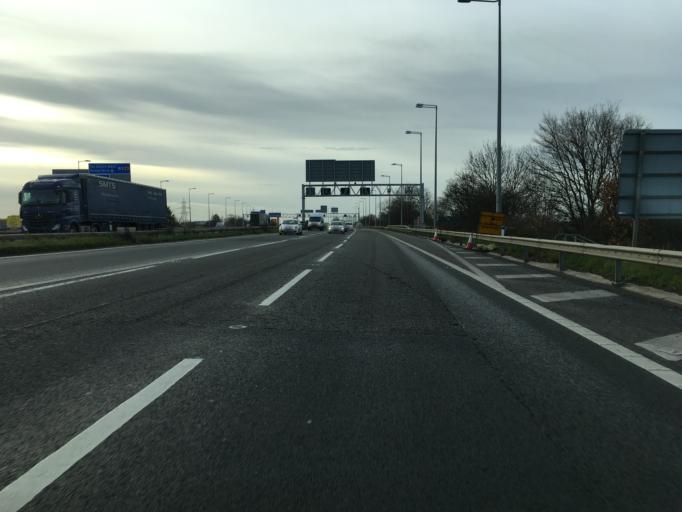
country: GB
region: England
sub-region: South Gloucestershire
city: Almondsbury
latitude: 51.5501
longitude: -2.5603
